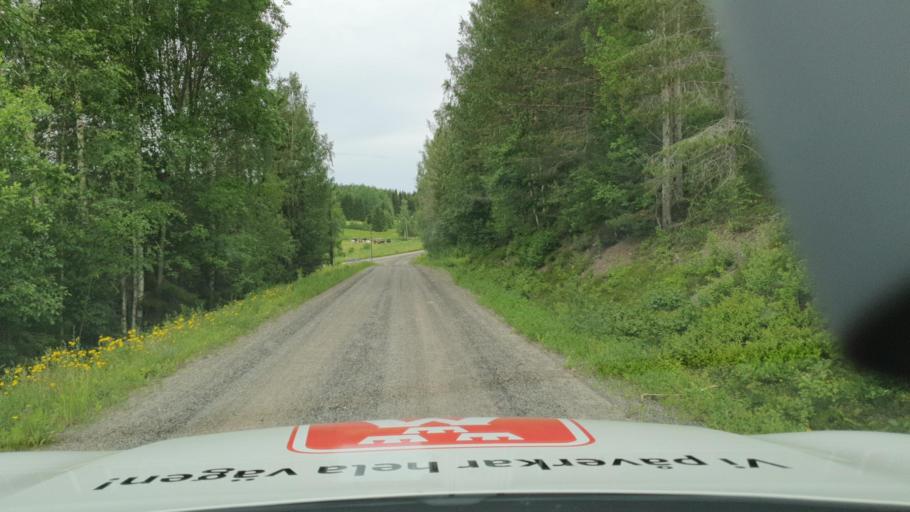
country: SE
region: Vaesterbotten
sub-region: Robertsfors Kommun
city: Robertsfors
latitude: 64.2150
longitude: 20.6869
